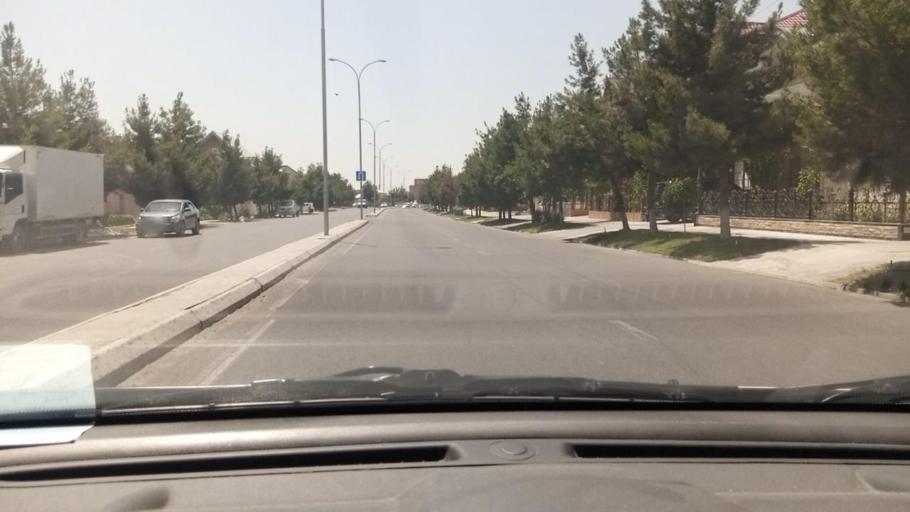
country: UZ
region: Toshkent Shahri
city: Tashkent
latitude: 41.2306
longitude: 69.1843
